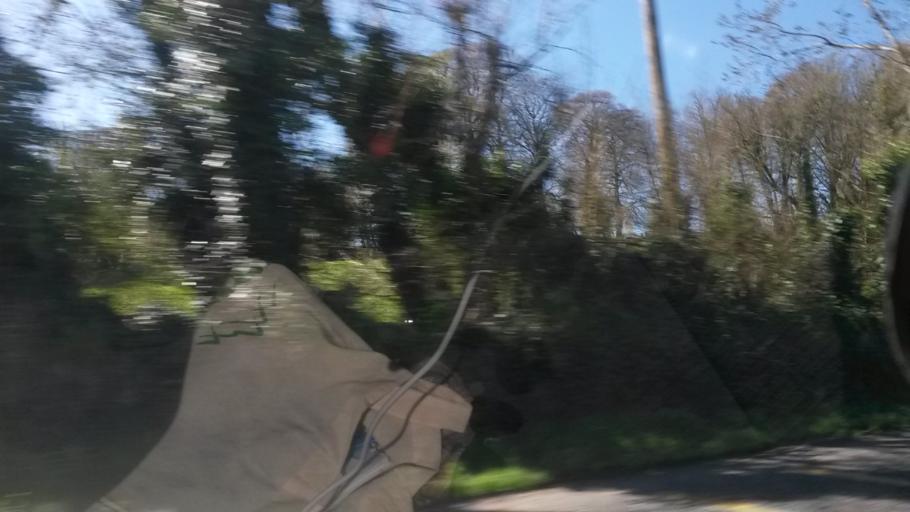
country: IE
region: Munster
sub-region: County Cork
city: Blarney
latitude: 51.8970
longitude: -8.5545
